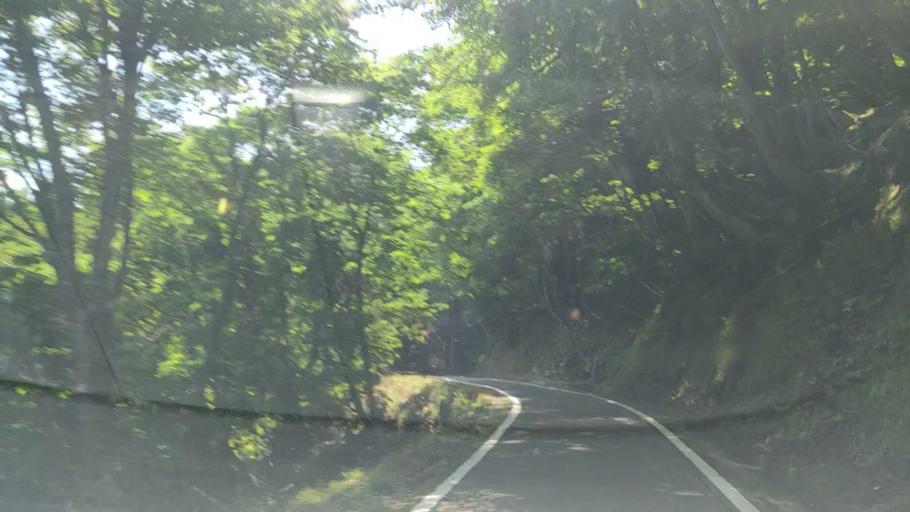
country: JP
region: Tottori
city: Tottori
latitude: 35.3762
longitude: 134.4903
